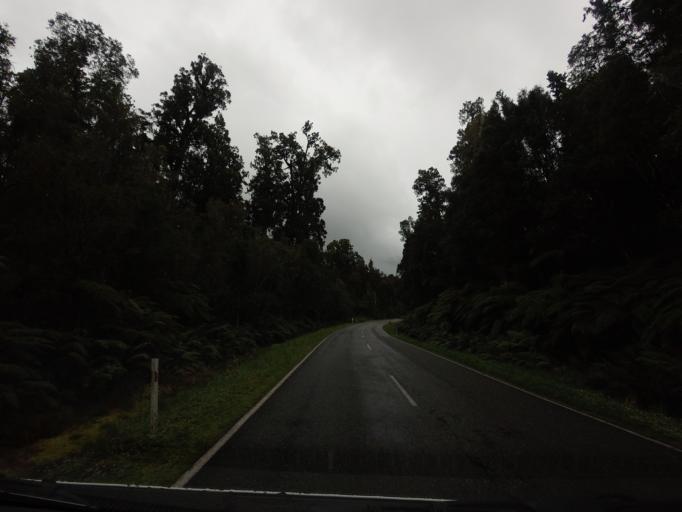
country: NZ
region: West Coast
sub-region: Westland District
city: Hokitika
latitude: -43.0278
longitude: 170.6613
